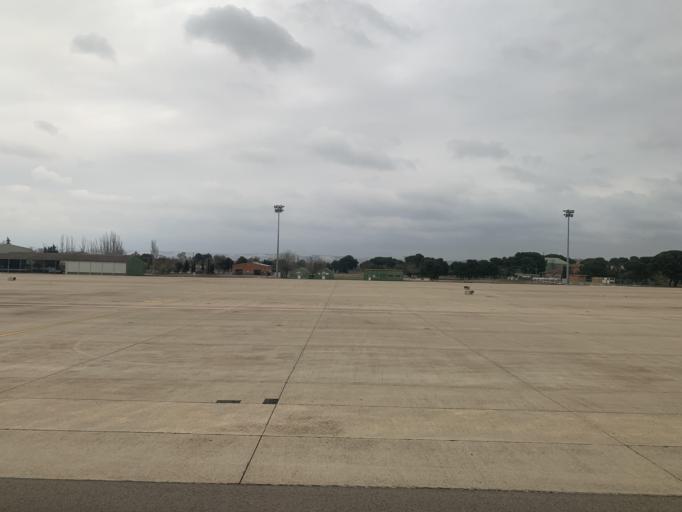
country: ES
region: Aragon
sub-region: Provincia de Zaragoza
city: Utebo
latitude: 41.6699
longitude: -1.0350
